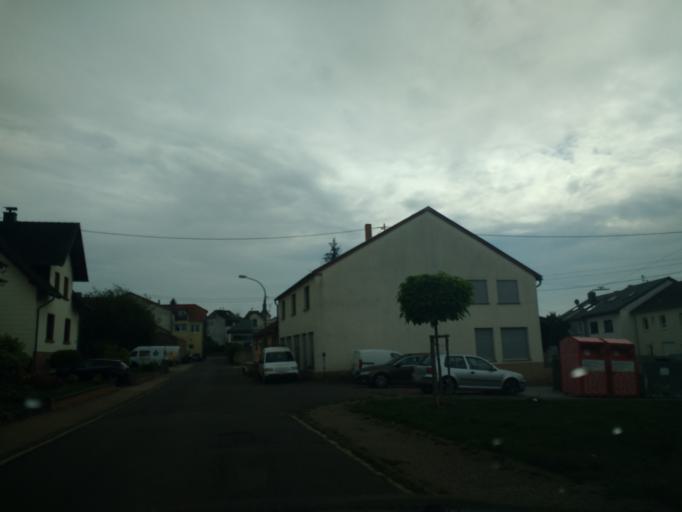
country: DE
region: Saarland
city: Orscholz
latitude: 49.5051
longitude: 6.5220
